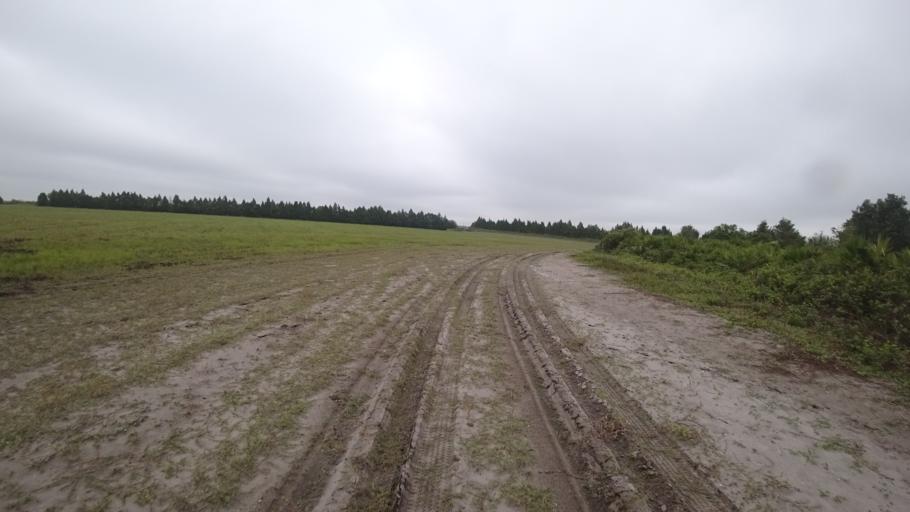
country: US
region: Florida
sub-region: Sarasota County
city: Warm Mineral Springs
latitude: 27.3076
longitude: -82.1484
